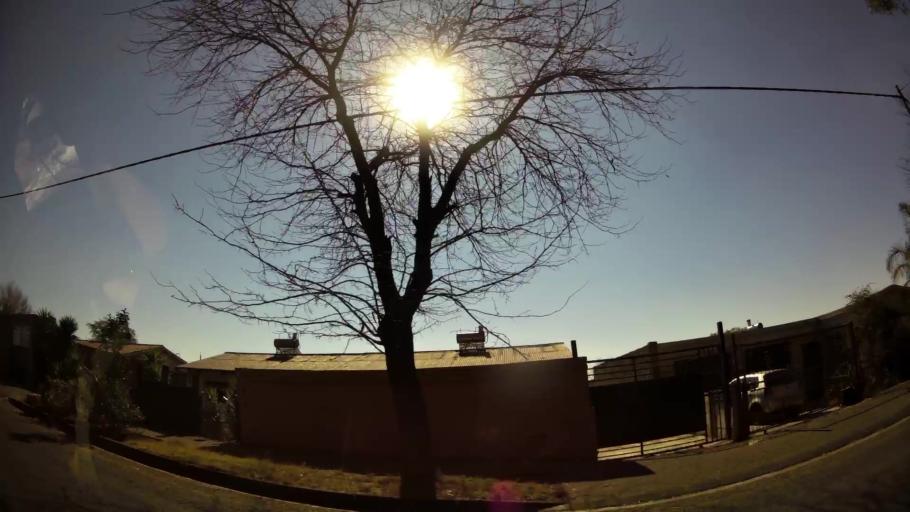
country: ZA
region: Gauteng
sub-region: City of Johannesburg Metropolitan Municipality
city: Roodepoort
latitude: -26.1791
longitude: 27.9573
